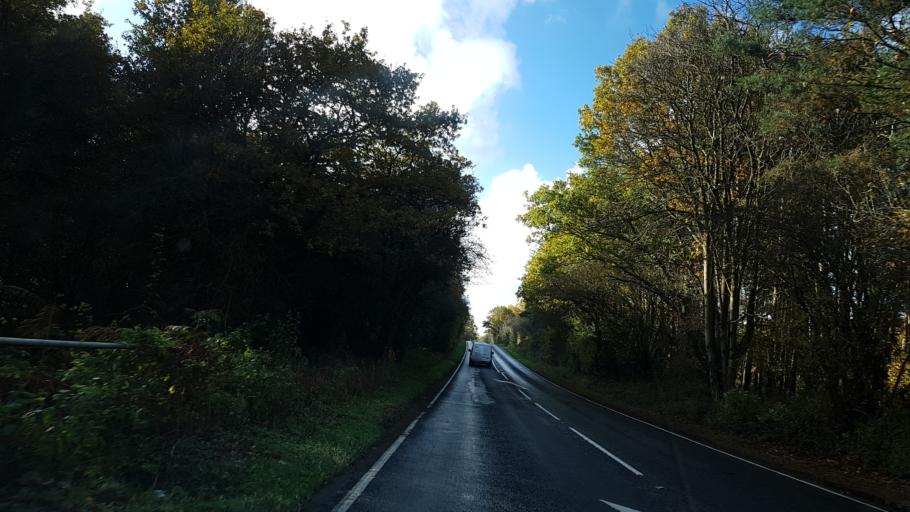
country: GB
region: England
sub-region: Surrey
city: Milford
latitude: 51.1627
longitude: -0.6578
